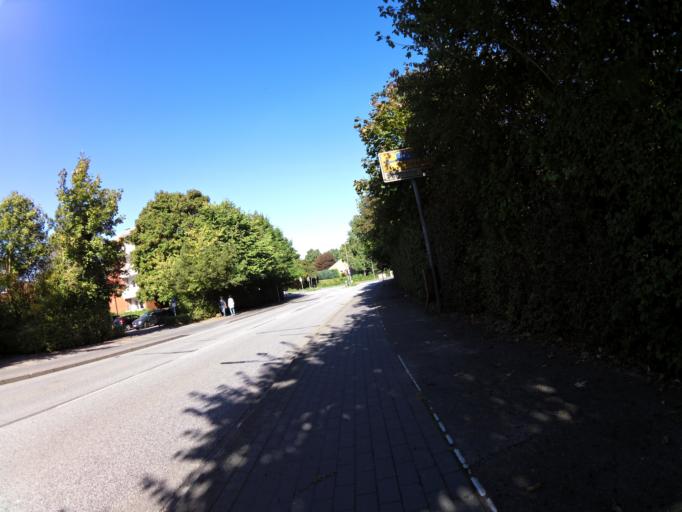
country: DE
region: Schleswig-Holstein
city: Windeby
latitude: 54.4598
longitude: 9.8274
